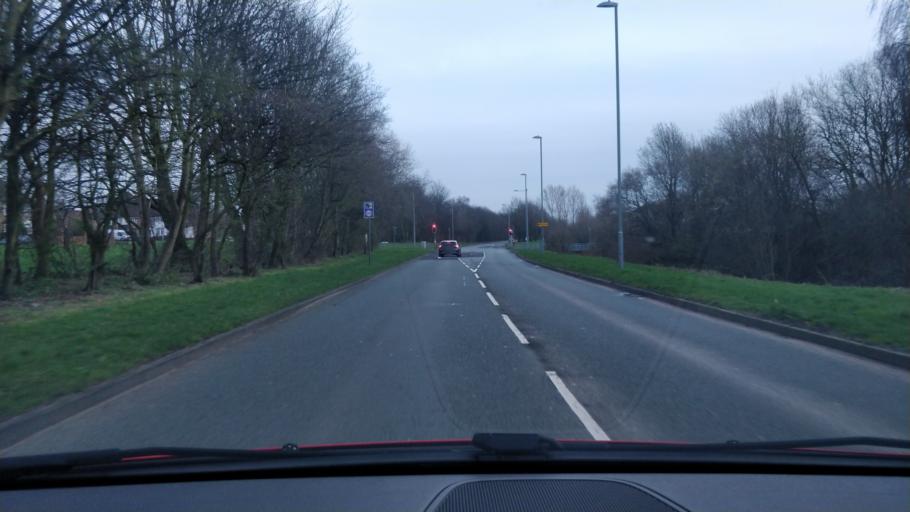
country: GB
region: England
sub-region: Knowsley
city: Huyton
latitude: 53.4254
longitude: -2.8509
